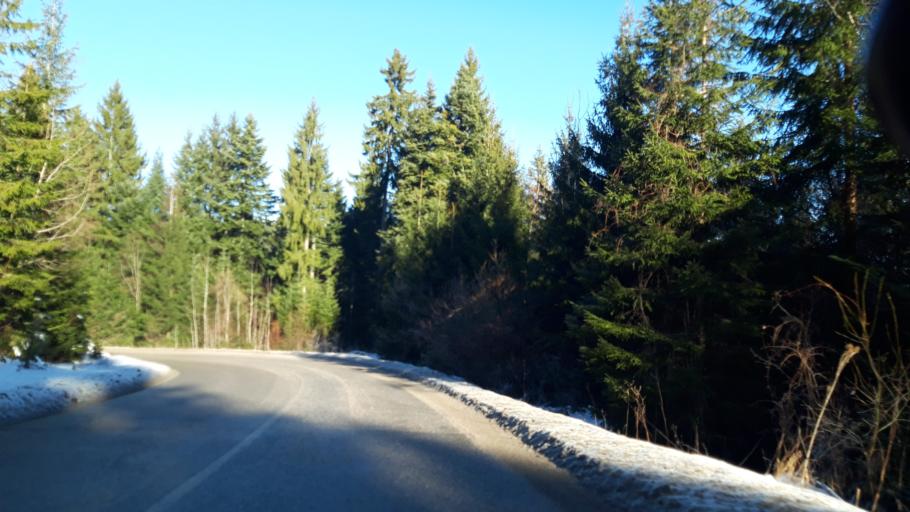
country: BA
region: Republika Srpska
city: Koran
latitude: 43.8010
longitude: 18.5504
